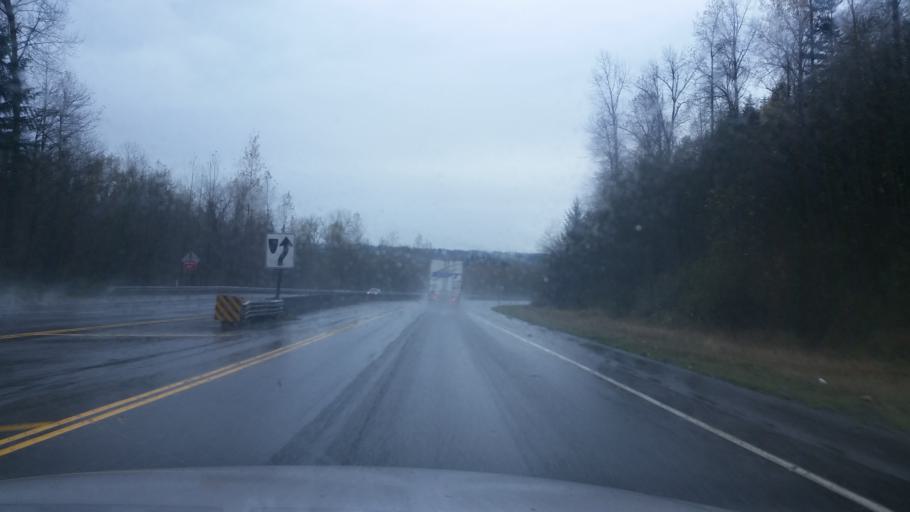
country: US
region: Washington
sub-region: King County
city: Hobart
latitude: 47.4386
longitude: -121.9643
